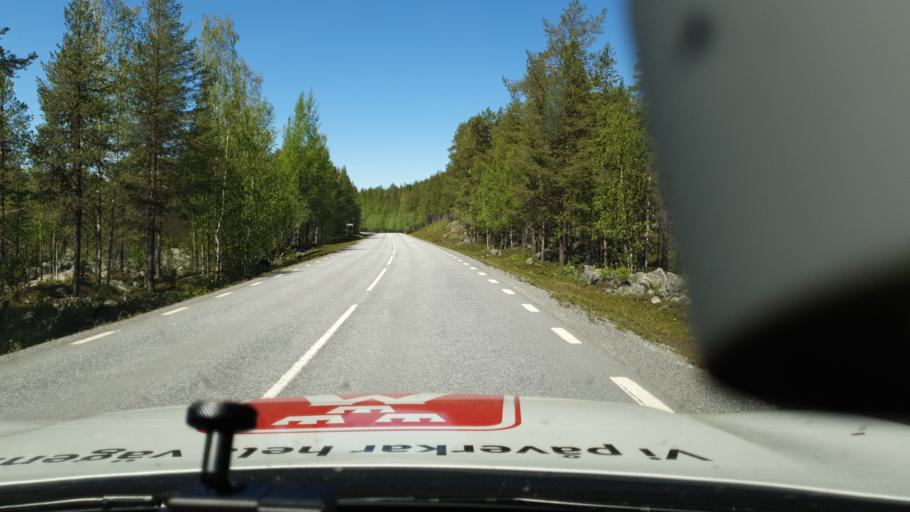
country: SE
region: Vaesterbotten
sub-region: Storumans Kommun
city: Storuman
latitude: 65.1573
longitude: 17.0594
